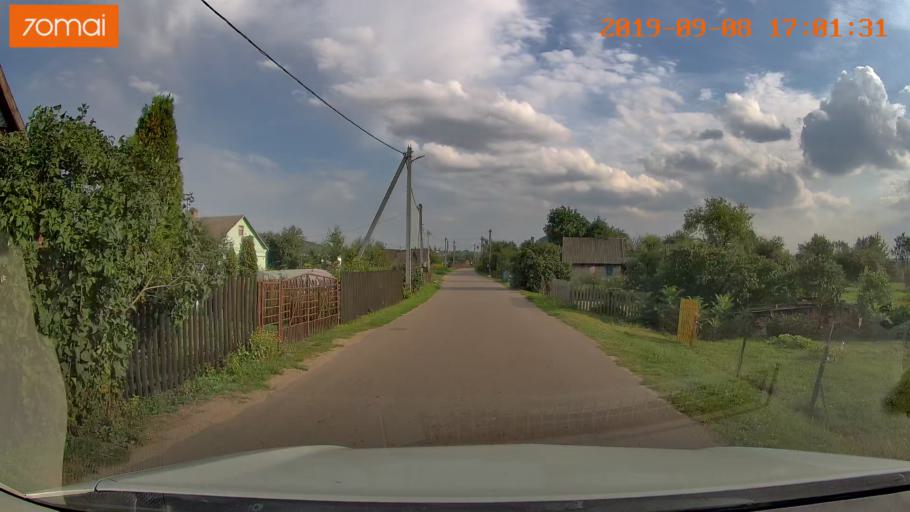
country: BY
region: Grodnenskaya
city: Hrodna
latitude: 53.7099
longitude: 23.9352
